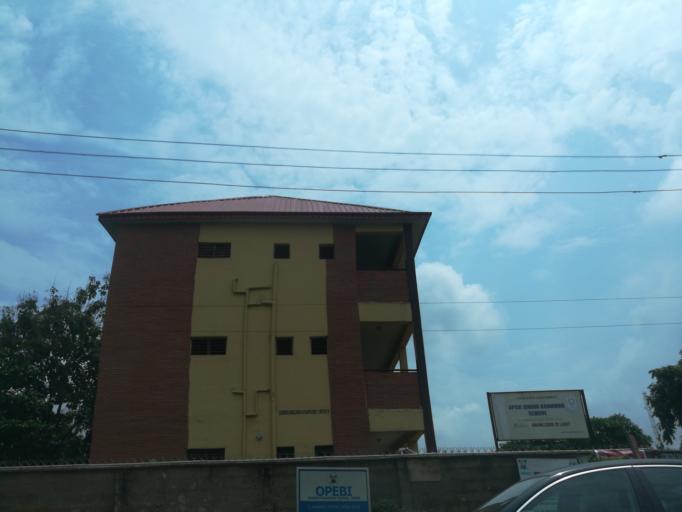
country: NG
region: Lagos
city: Ojota
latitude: 6.5892
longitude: 3.3626
